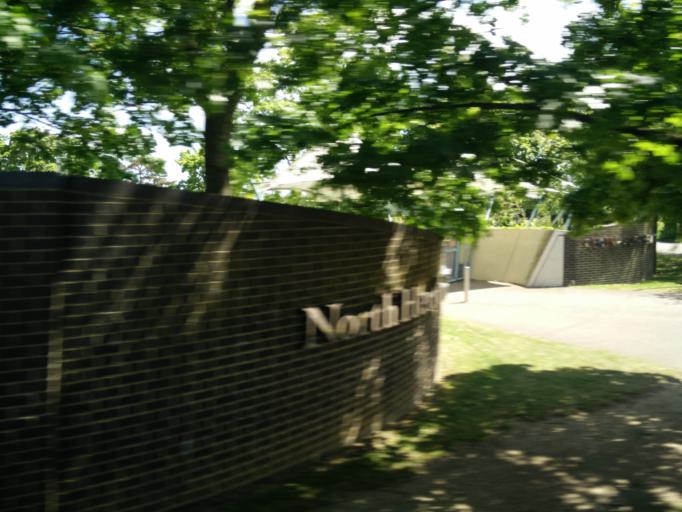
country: GB
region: England
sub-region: Hertfordshire
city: Hitchin
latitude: 51.9566
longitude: -0.2563
